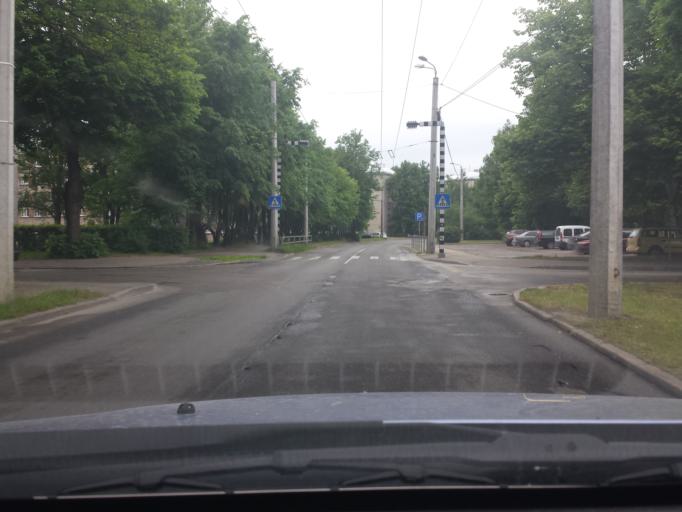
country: LV
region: Riga
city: Jaunciems
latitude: 56.9753
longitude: 24.1866
